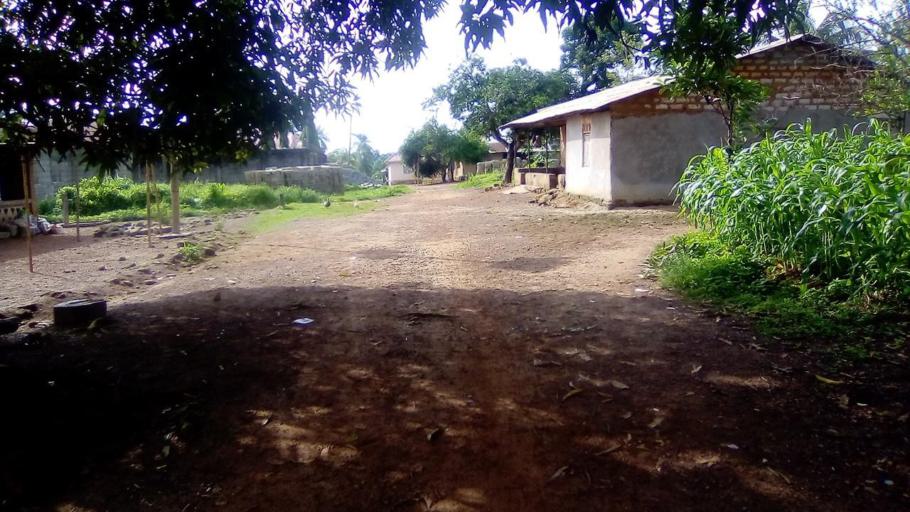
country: SL
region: Southern Province
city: Pujehun
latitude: 7.3601
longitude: -11.7227
